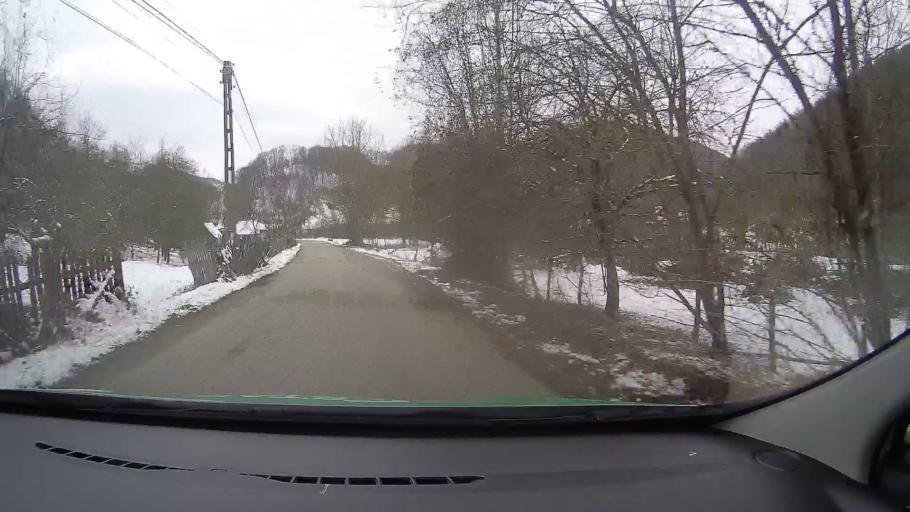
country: RO
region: Hunedoara
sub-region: Comuna Balsa
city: Balsa
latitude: 46.0480
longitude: 23.0699
